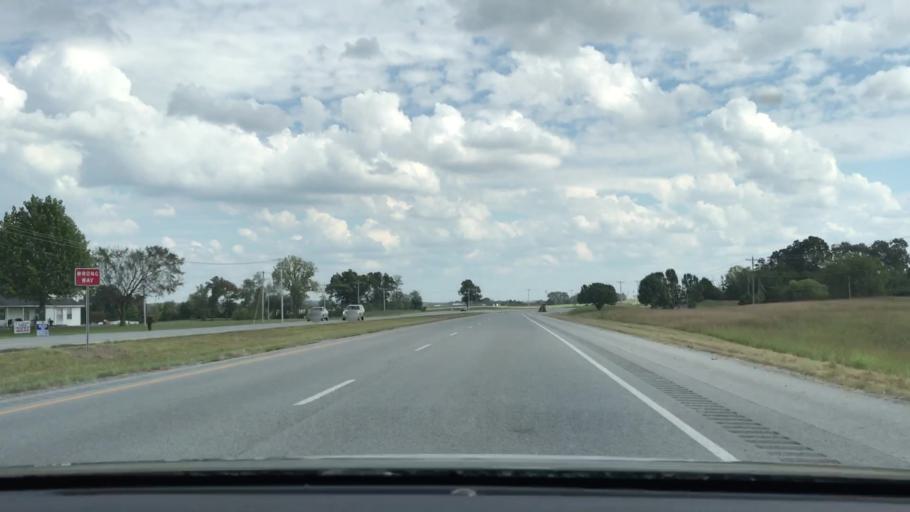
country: US
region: Kentucky
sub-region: Trigg County
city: Cadiz
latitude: 36.8750
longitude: -87.7546
